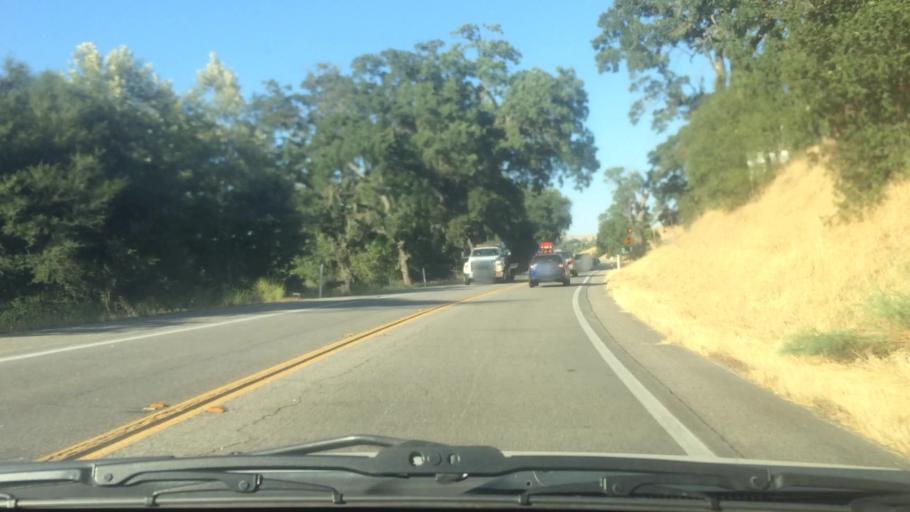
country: US
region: California
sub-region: San Luis Obispo County
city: Atascadero
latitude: 35.4613
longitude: -120.6779
